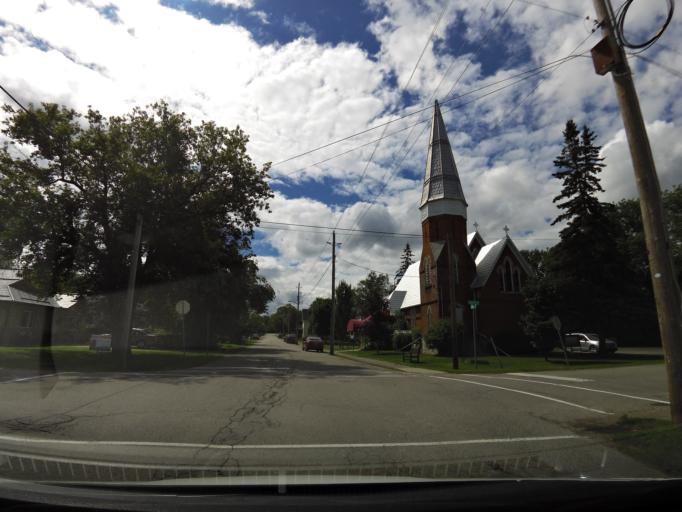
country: CA
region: Ontario
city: Perth
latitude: 44.6780
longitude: -76.3981
